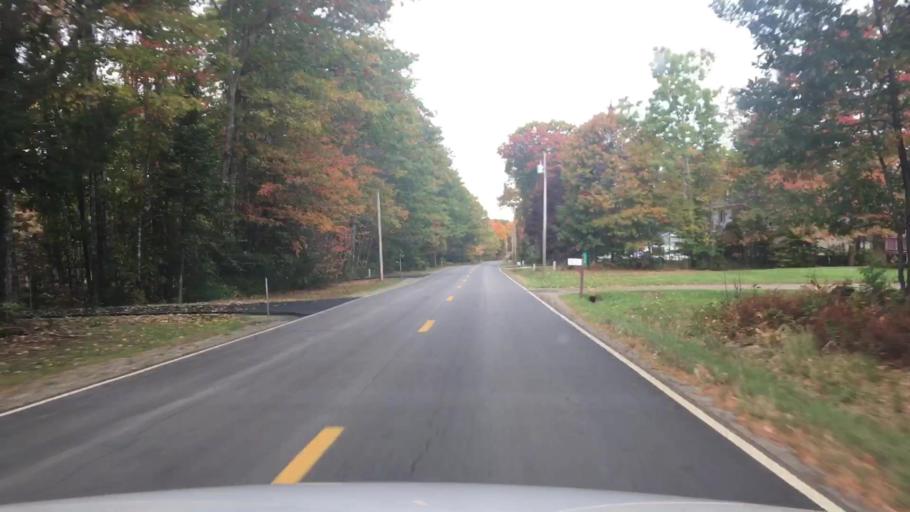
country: US
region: Maine
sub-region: Waldo County
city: Searsmont
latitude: 44.4150
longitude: -69.1385
